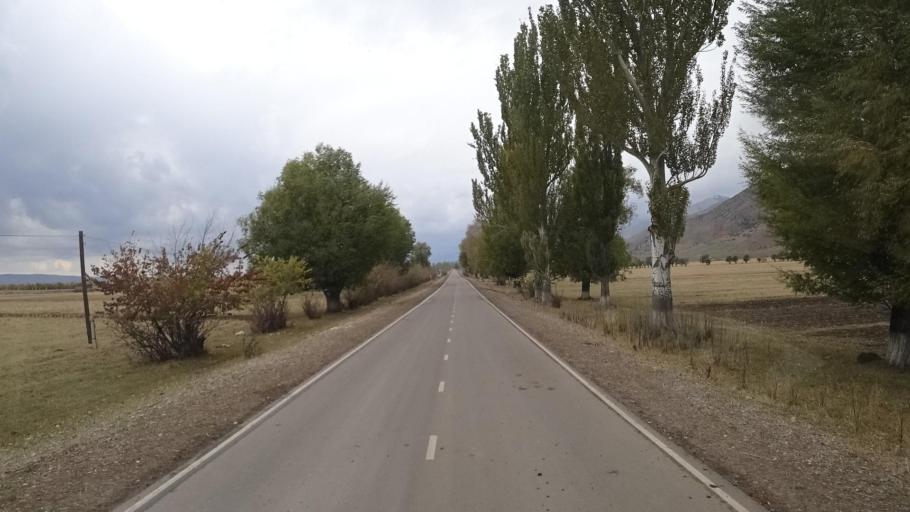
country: KG
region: Ysyk-Koel
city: Teploklyuchenka
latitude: 42.7565
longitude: 78.6809
